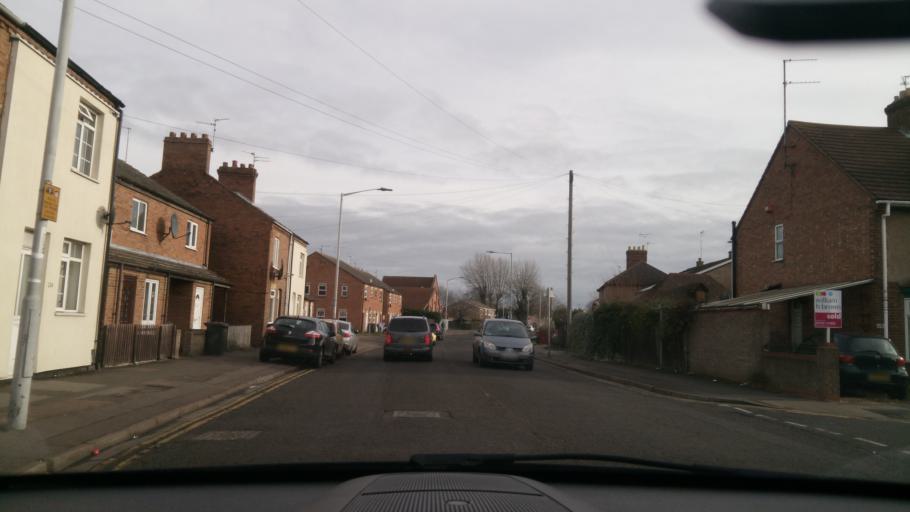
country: GB
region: England
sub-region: Peterborough
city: Peterborough
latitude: 52.5960
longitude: -0.2450
